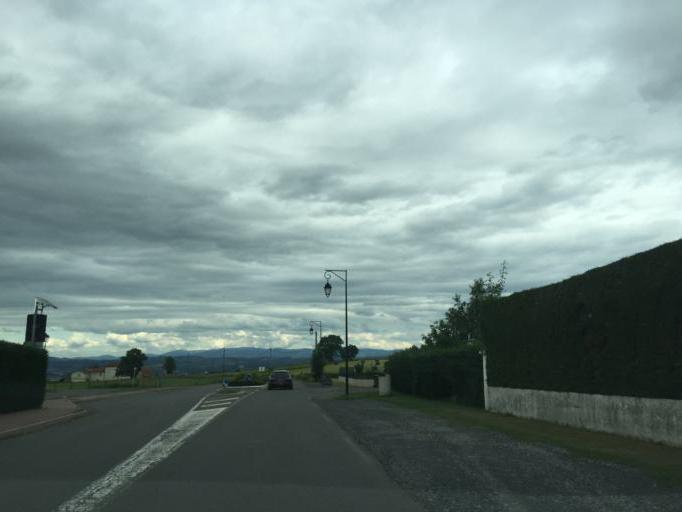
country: FR
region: Rhone-Alpes
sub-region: Departement de la Loire
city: Saint-Georges-Haute-Ville
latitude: 45.5121
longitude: 4.1057
